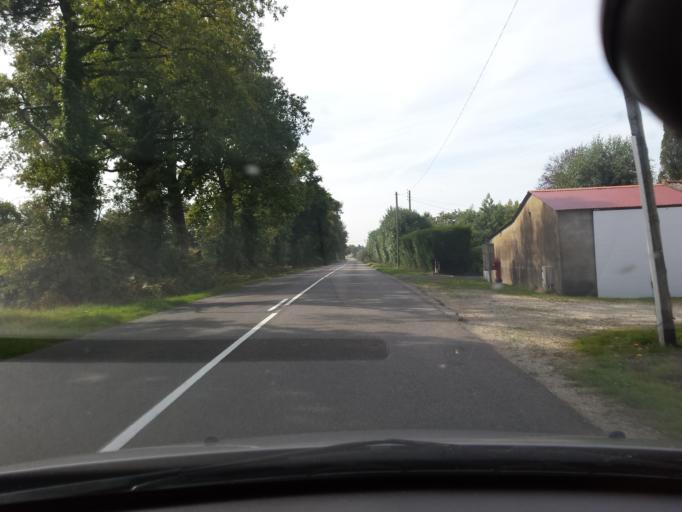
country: FR
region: Pays de la Loire
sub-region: Departement de la Vendee
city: Aubigny
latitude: 46.5915
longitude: -1.4689
